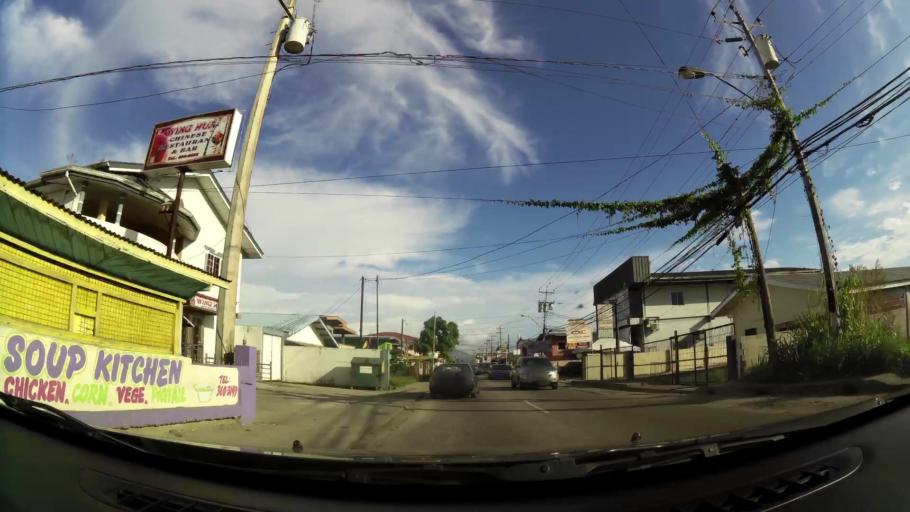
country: TT
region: Chaguanas
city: Chaguanas
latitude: 10.5650
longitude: -61.3733
